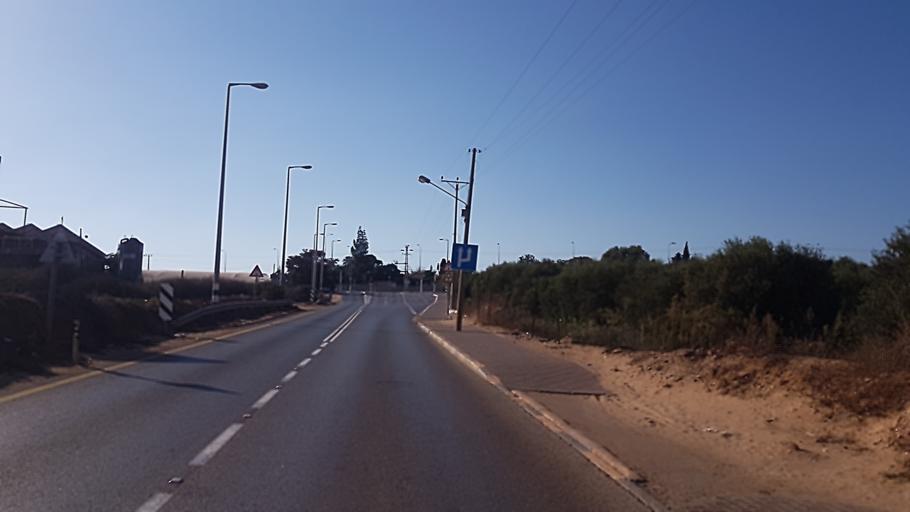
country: IL
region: Central District
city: Kfar Saba
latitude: 32.1988
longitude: 34.9180
